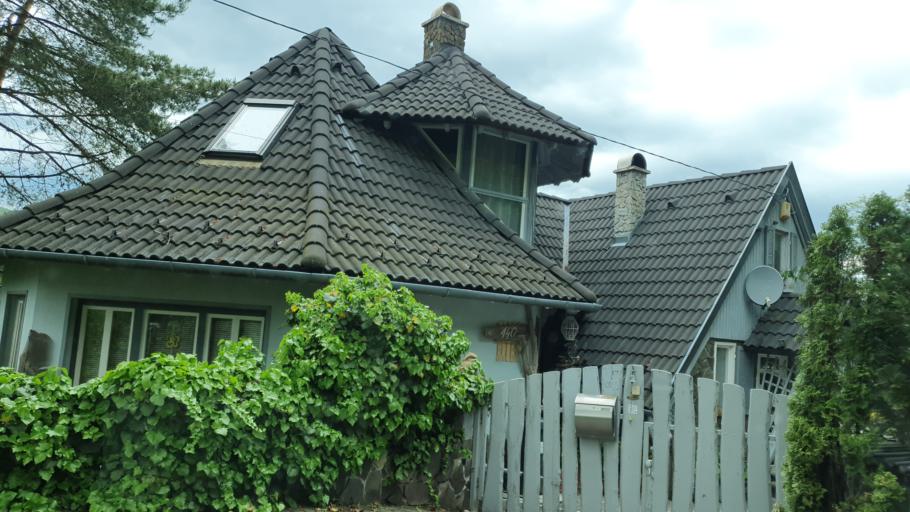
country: HU
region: Komarom-Esztergom
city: Esztergom
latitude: 47.8132
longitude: 18.7951
